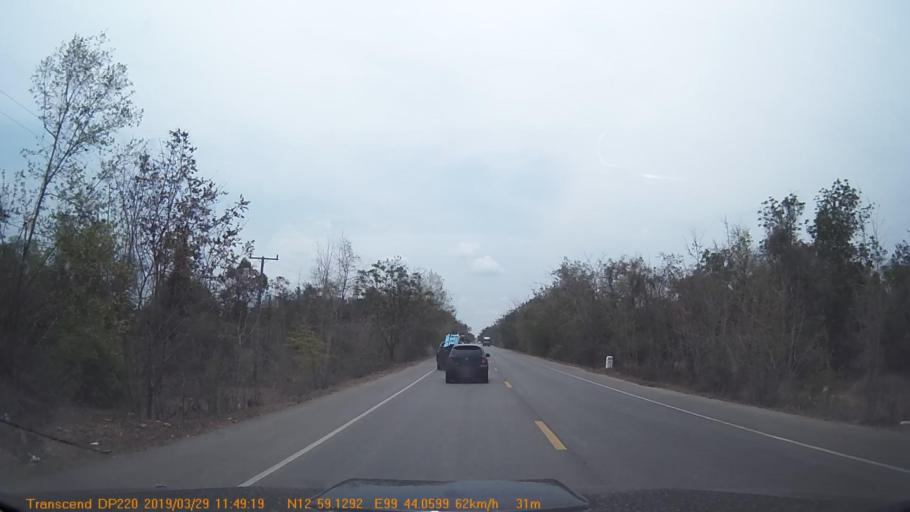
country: TH
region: Phetchaburi
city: Kaeng Krachan
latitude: 12.9852
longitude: 99.7344
